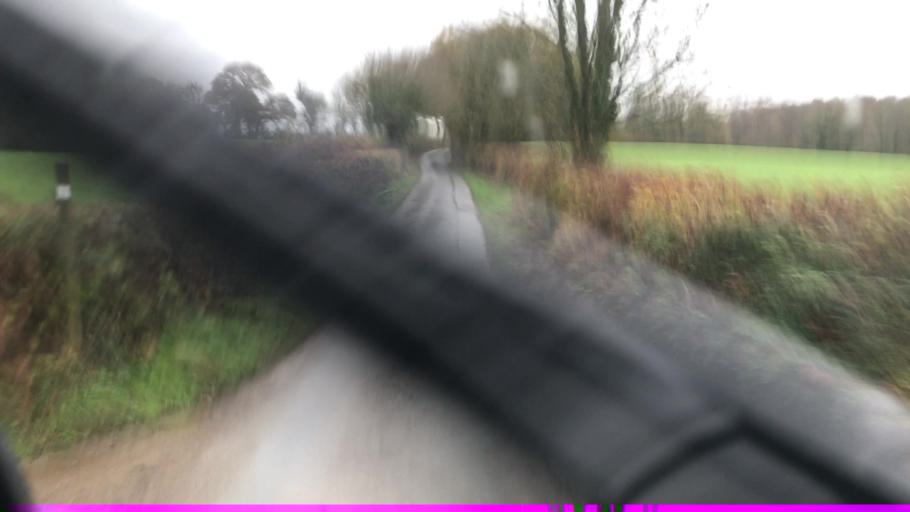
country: GB
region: England
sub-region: Devon
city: Chudleigh
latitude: 50.6397
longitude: -3.6122
